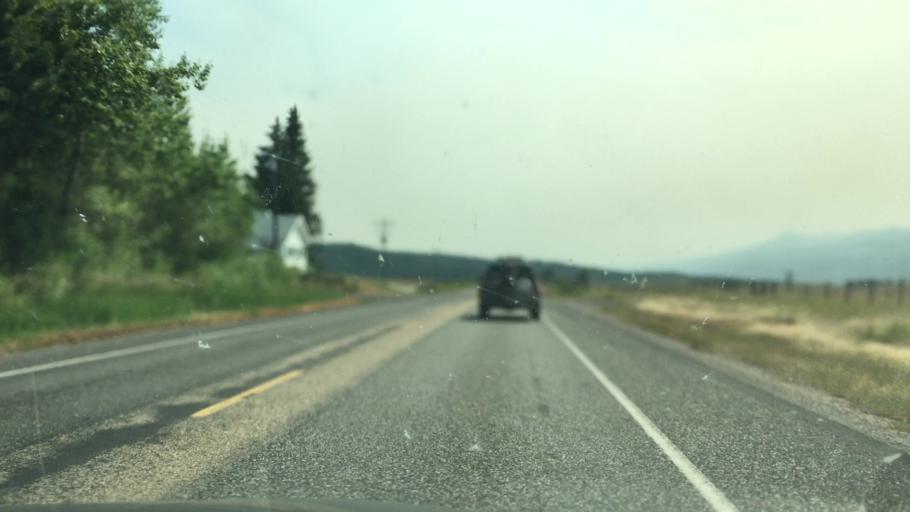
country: US
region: Idaho
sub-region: Valley County
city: Cascade
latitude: 44.6103
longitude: -116.0485
